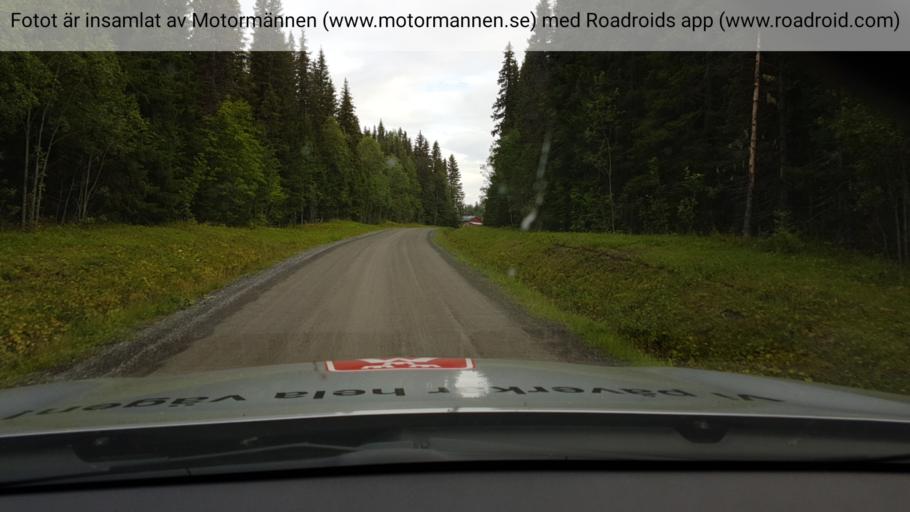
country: SE
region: Jaemtland
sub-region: OEstersunds Kommun
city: Lit
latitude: 63.6468
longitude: 14.9503
